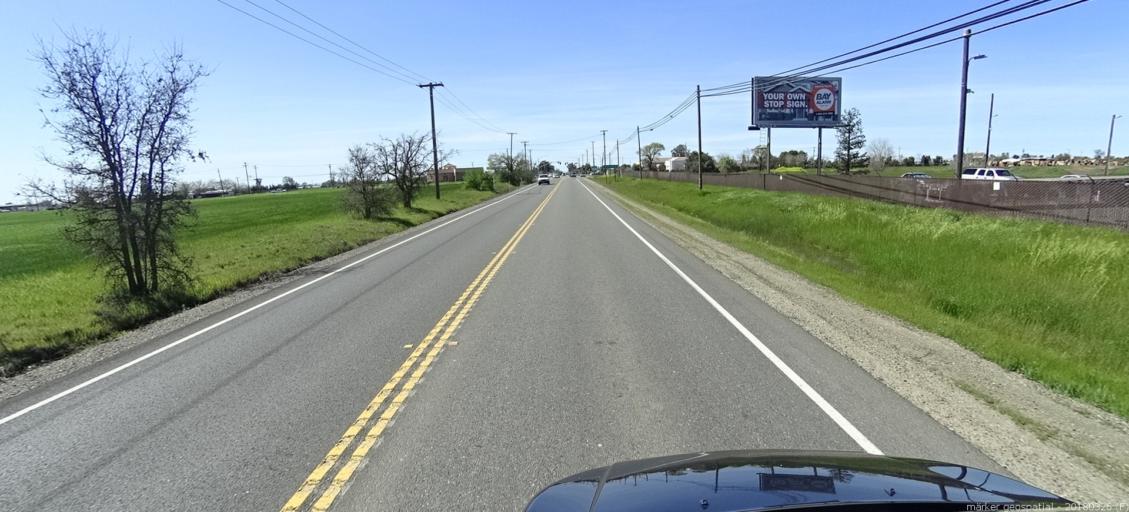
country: US
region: California
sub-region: Sacramento County
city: Rosemont
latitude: 38.5281
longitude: -121.3316
